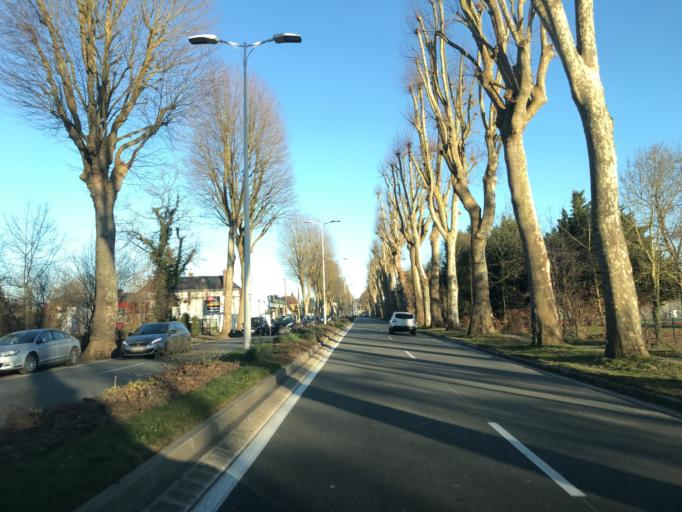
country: FR
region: Haute-Normandie
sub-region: Departement de l'Eure
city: Evreux
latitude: 49.0238
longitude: 1.1294
